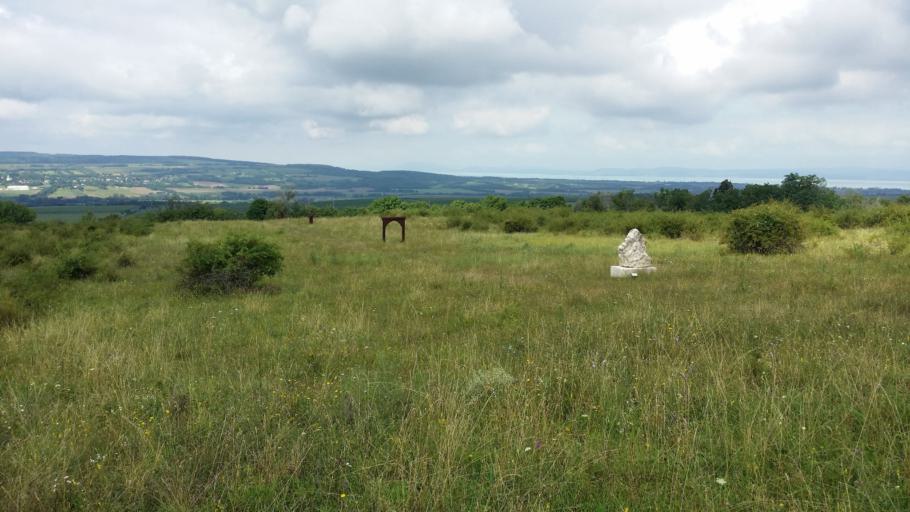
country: HU
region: Somogy
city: Balatonszarszo
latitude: 46.7825
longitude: 17.8757
